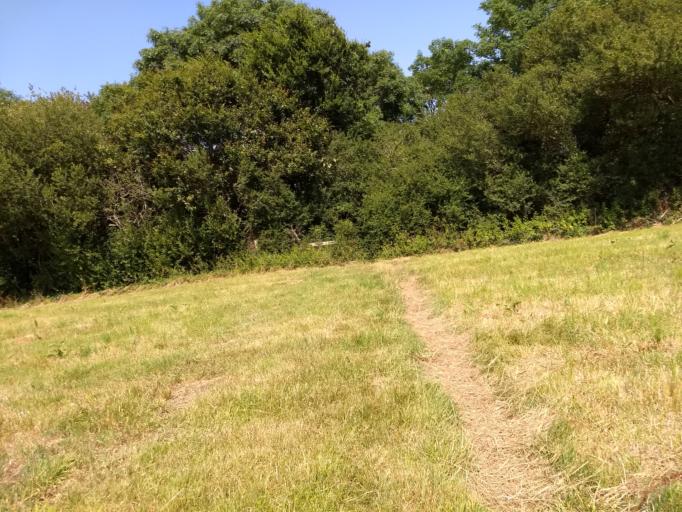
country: GB
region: England
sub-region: Isle of Wight
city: Northwood
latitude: 50.7340
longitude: -1.3218
